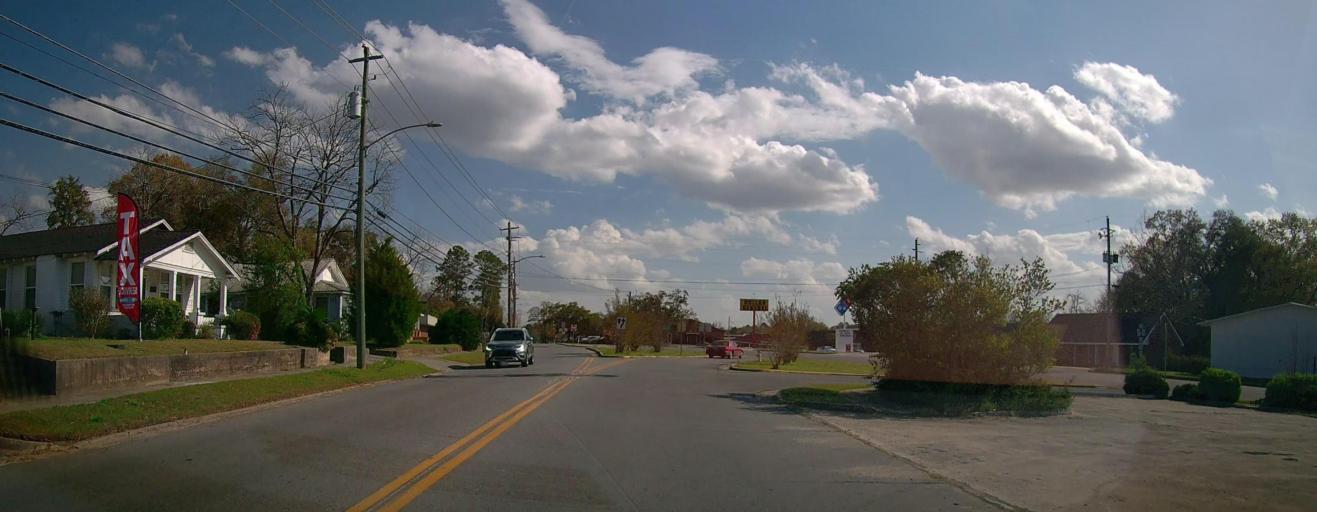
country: US
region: Georgia
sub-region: Dodge County
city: Eastman
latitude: 32.1925
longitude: -83.1745
